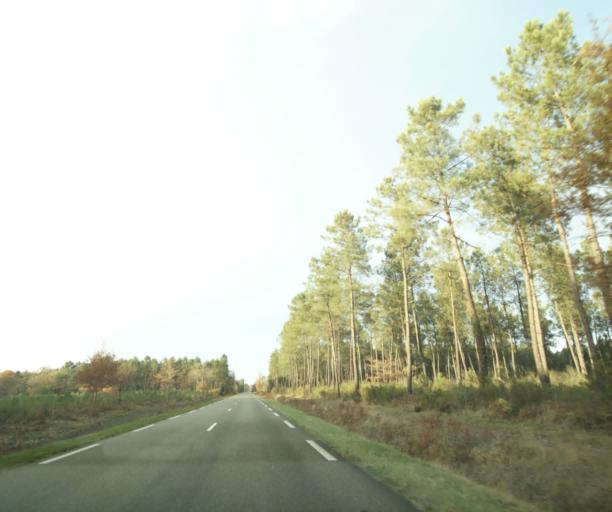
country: FR
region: Aquitaine
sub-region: Departement des Landes
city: Gabarret
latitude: 44.0455
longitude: -0.0389
